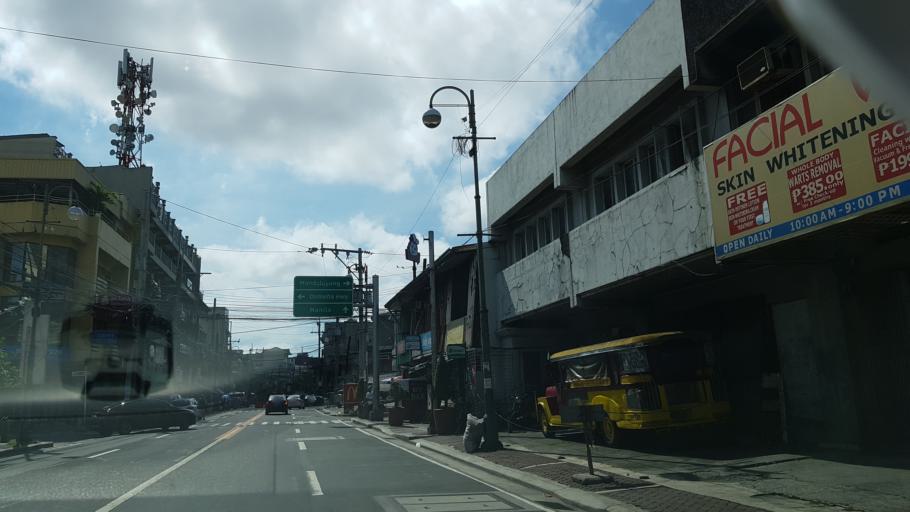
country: PH
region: Metro Manila
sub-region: Makati City
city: Makati City
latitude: 14.5716
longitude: 121.0167
